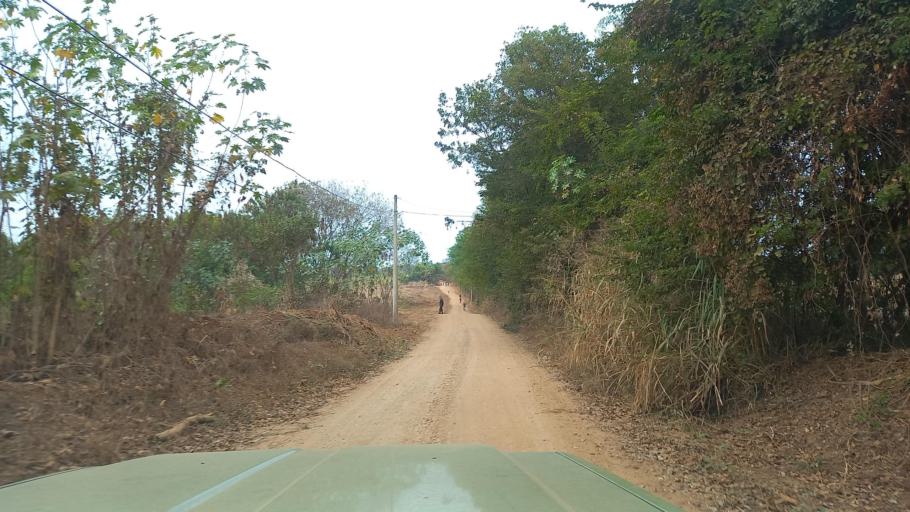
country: BR
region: Sao Paulo
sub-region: Moji-Guacu
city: Mogi-Gaucu
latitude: -22.2840
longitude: -46.8449
